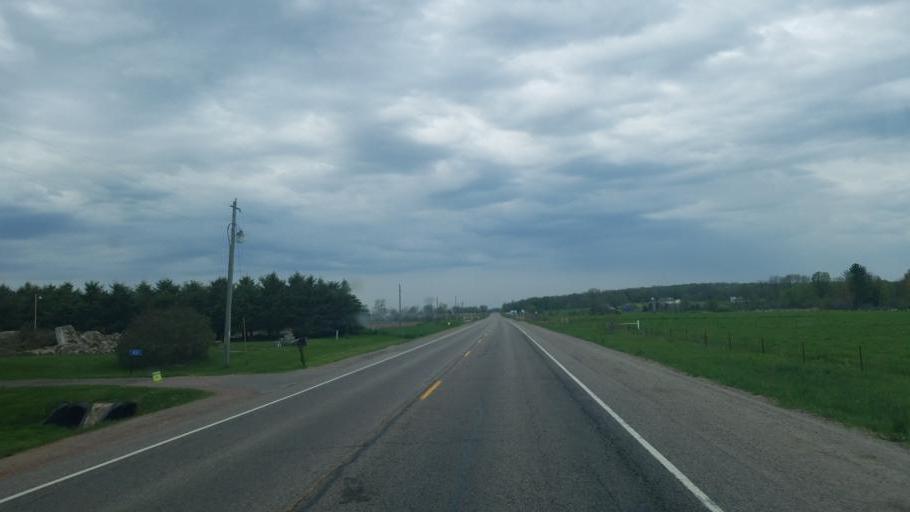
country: US
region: Wisconsin
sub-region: Marathon County
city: Spencer
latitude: 44.5988
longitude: -90.3254
